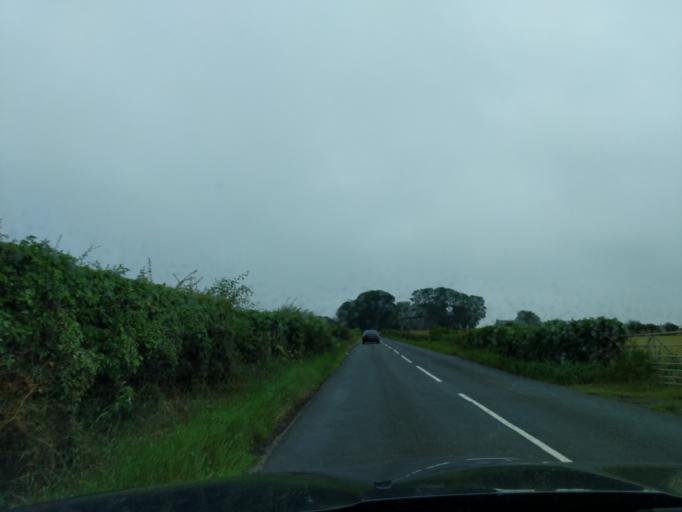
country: GB
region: England
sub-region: Northumberland
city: Lowick
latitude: 55.6557
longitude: -1.9155
